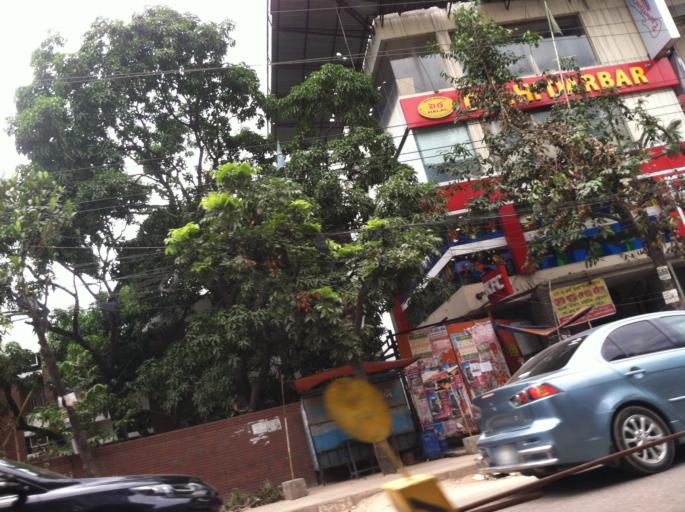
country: BD
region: Dhaka
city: Paltan
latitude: 23.7520
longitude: 90.4168
